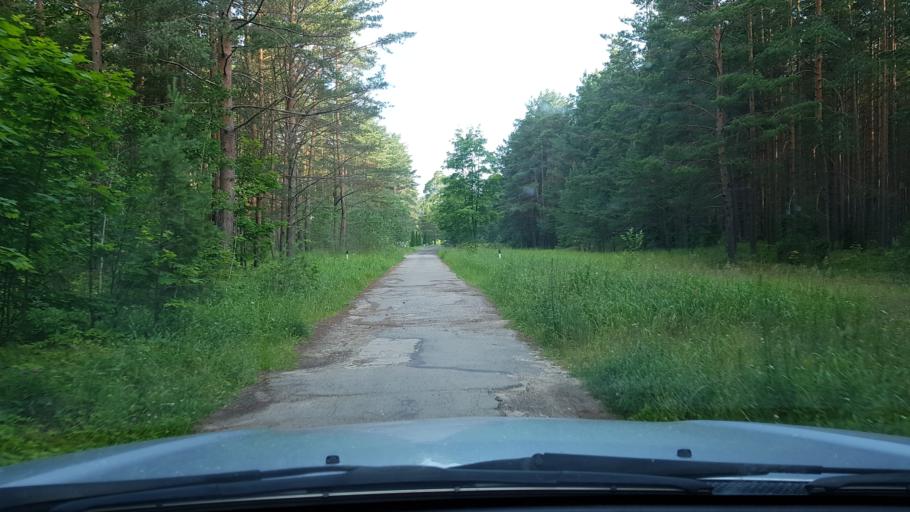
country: EE
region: Ida-Virumaa
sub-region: Narva-Joesuu linn
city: Narva-Joesuu
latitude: 59.4530
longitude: 28.0411
